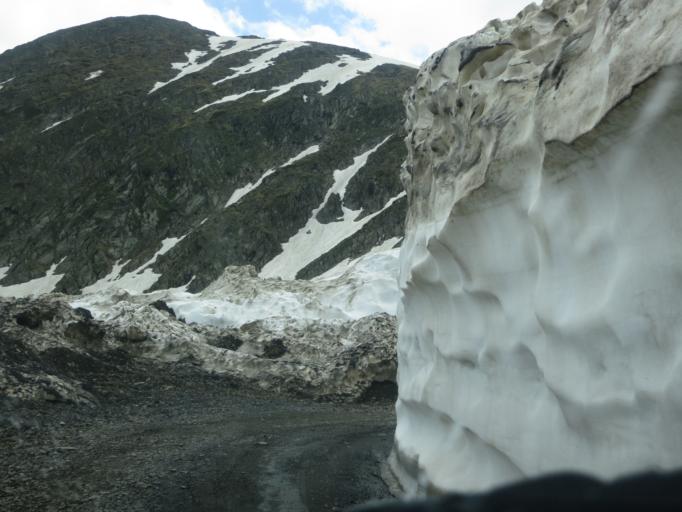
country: GE
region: Kakheti
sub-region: Telavi
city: Telavi
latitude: 42.2804
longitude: 45.5071
